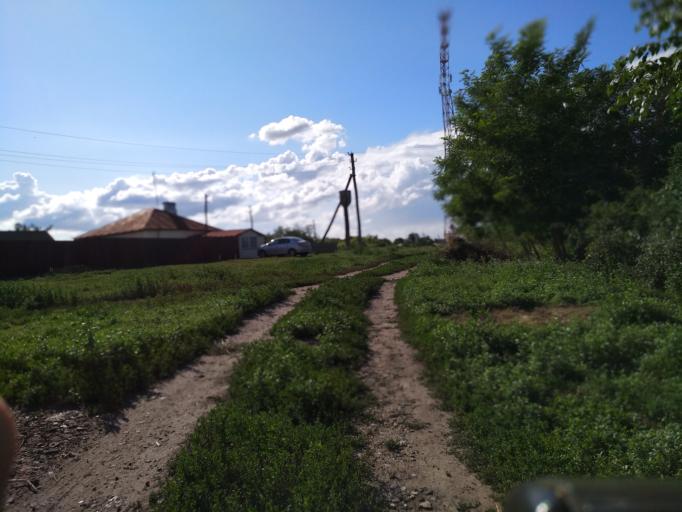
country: RU
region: Lipetsk
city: Dobrinka
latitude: 52.0353
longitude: 40.5586
